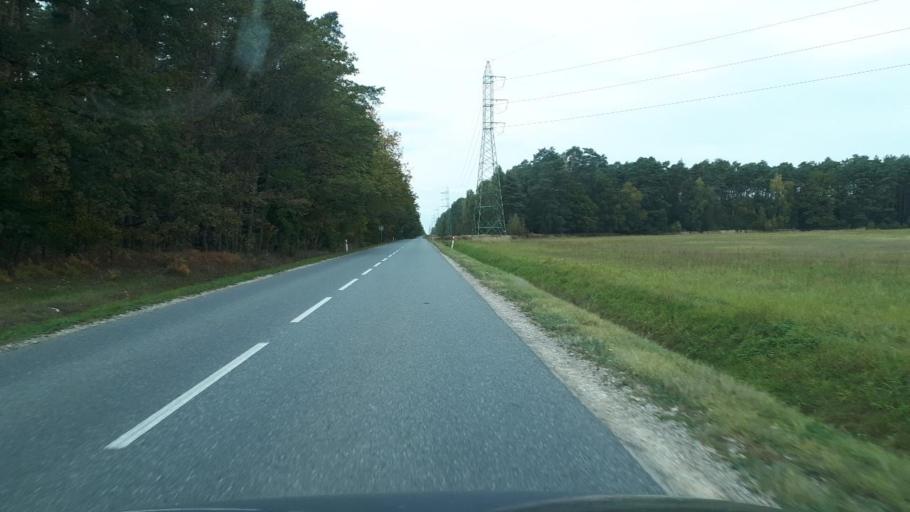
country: PL
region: Opole Voivodeship
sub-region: Powiat oleski
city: Dobrodzien
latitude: 50.7820
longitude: 18.4235
